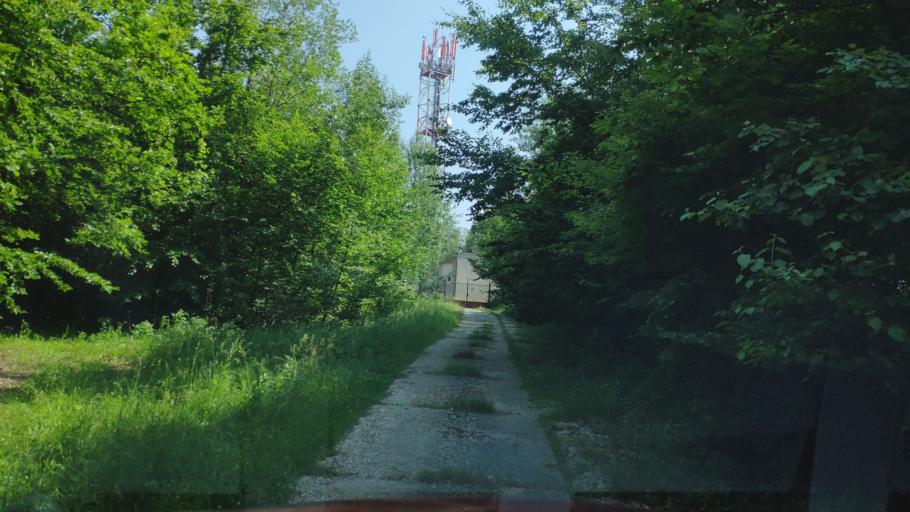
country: SK
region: Presovsky
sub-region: Okres Presov
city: Presov
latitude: 48.9711
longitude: 21.1499
